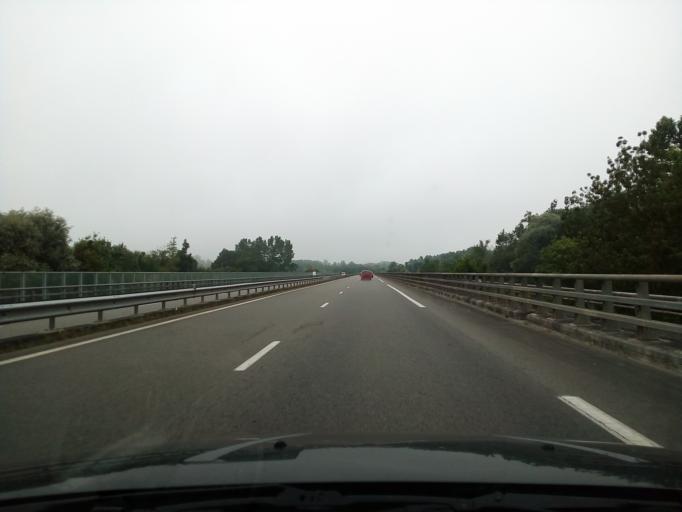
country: FR
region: Poitou-Charentes
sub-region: Departement de la Charente
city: Jarnac
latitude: 45.6732
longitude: -0.1593
